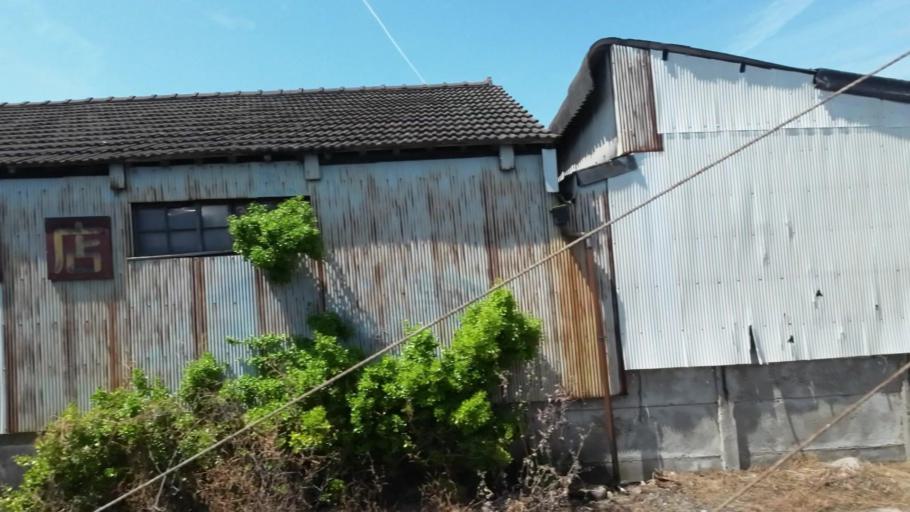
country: JP
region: Kagawa
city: Marugame
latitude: 34.2322
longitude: 133.7880
